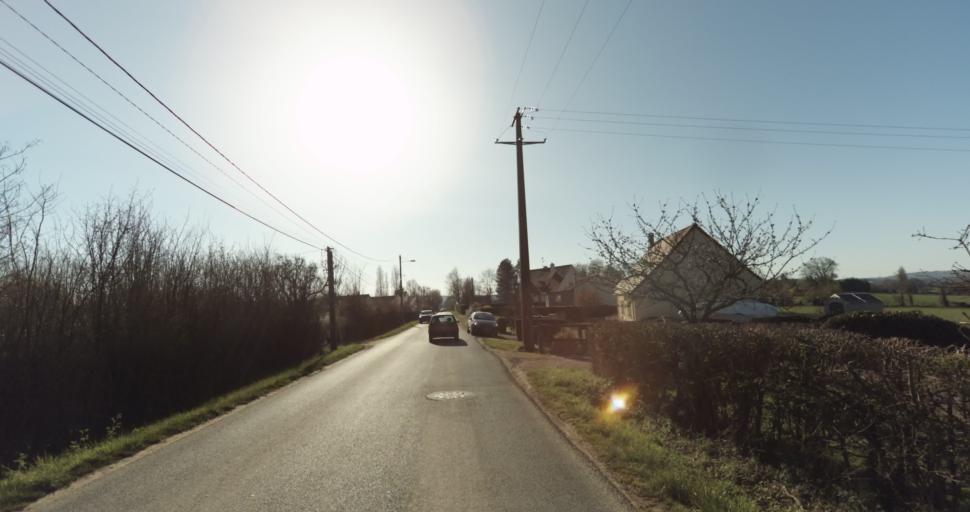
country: FR
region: Lower Normandy
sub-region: Departement du Calvados
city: Saint-Pierre-sur-Dives
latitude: 49.0051
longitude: -0.0093
